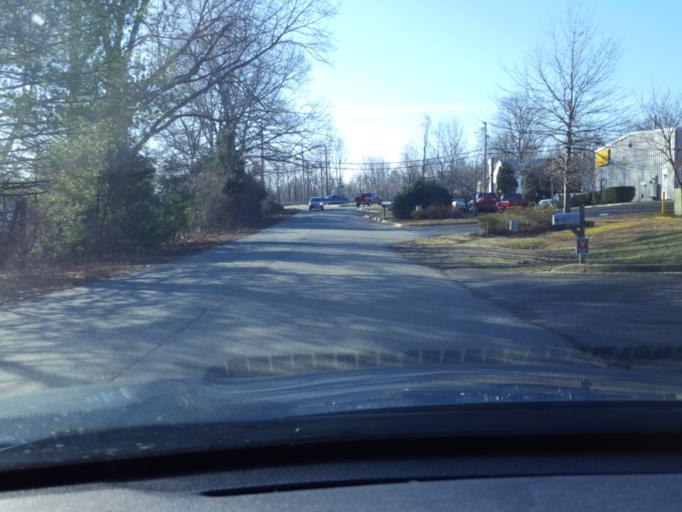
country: US
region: Maryland
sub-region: Calvert County
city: Owings
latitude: 38.7042
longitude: -76.5813
